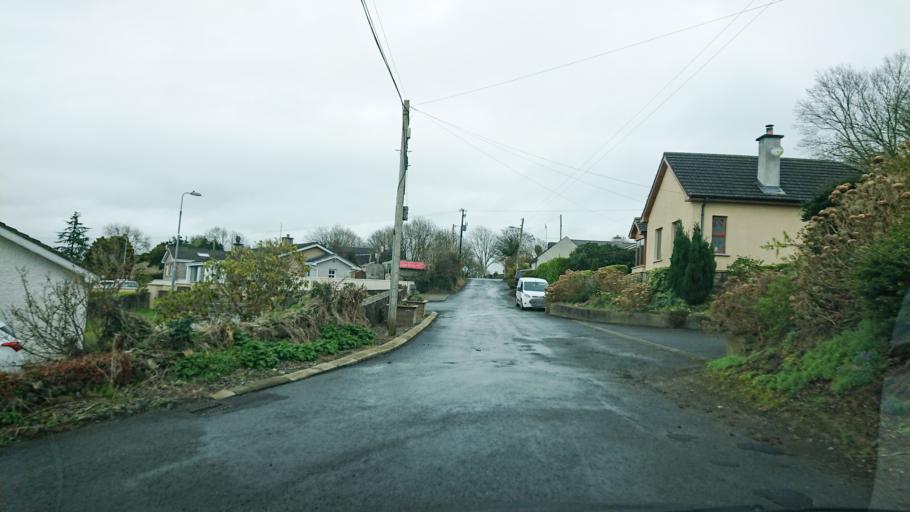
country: IE
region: Munster
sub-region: Waterford
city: Waterford
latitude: 52.2694
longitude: -6.9973
